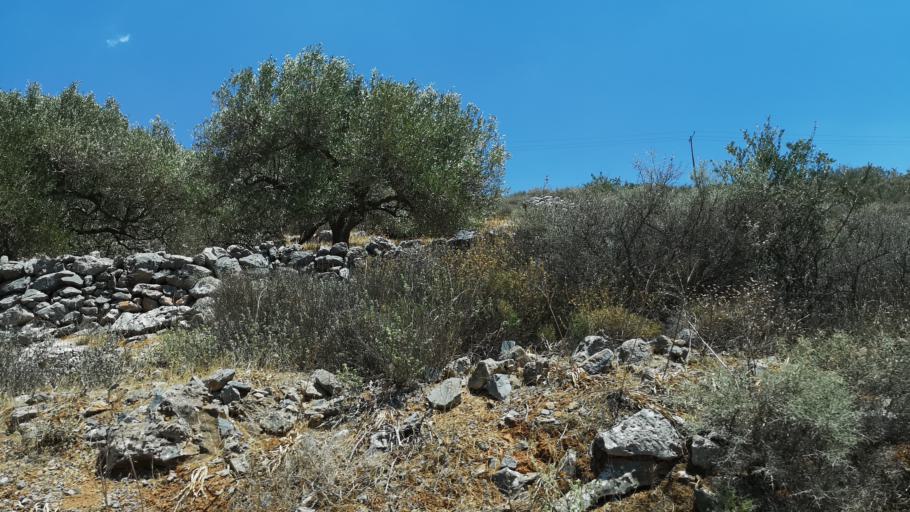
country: GR
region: Crete
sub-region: Nomos Lasithiou
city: Neapoli
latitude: 35.2566
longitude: 25.6412
